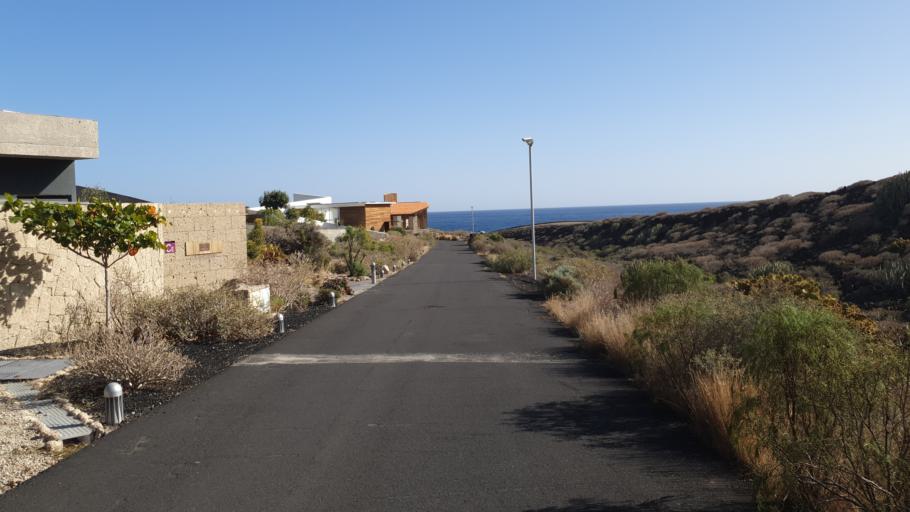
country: ES
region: Canary Islands
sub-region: Provincia de Santa Cruz de Tenerife
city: San Isidro
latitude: 28.0682
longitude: -16.5119
